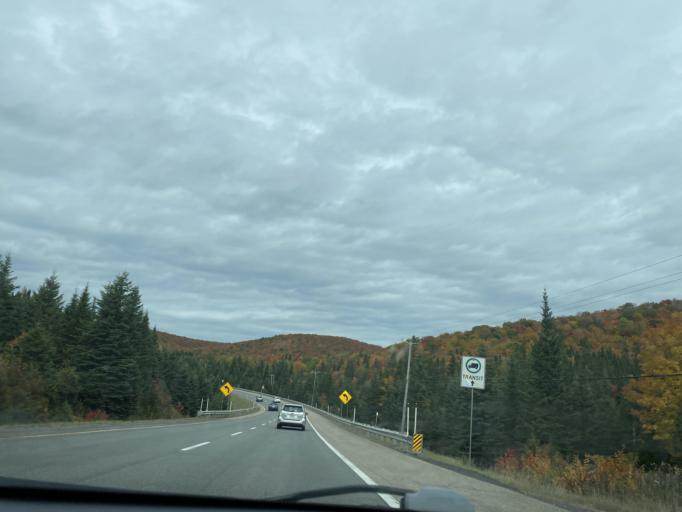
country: CA
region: Quebec
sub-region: Laurentides
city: Sainte-Agathe-des-Monts
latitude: 46.1205
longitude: -74.4318
